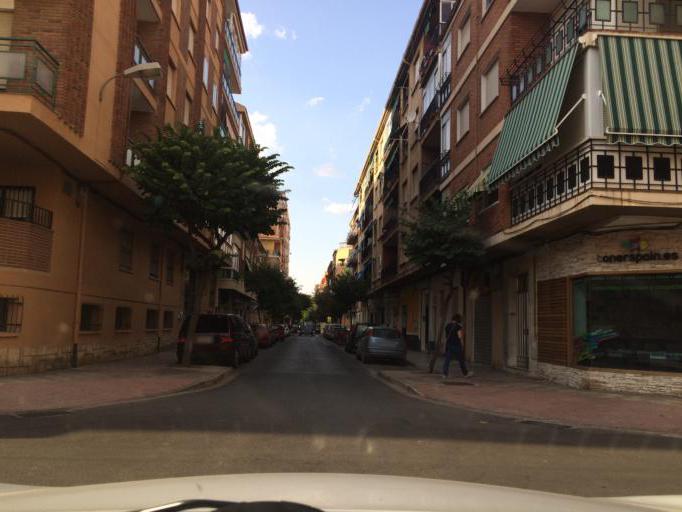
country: ES
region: Castille-La Mancha
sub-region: Provincia de Albacete
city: Albacete
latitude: 38.9929
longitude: -1.8653
